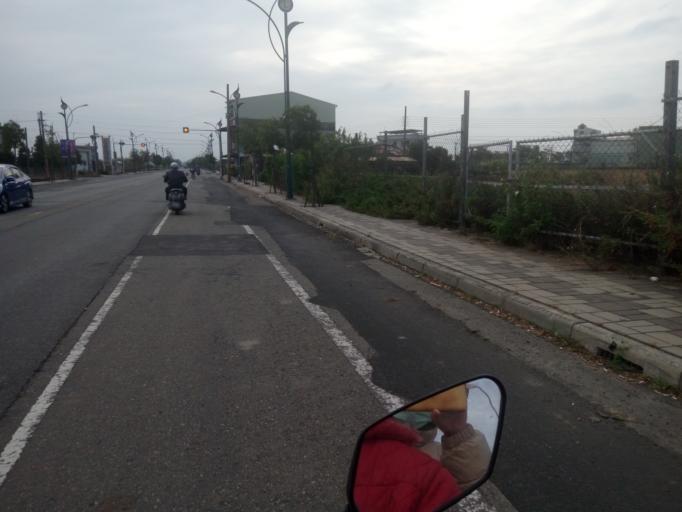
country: TW
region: Taiwan
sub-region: Chiayi
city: Taibao
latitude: 23.4959
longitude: 120.3604
